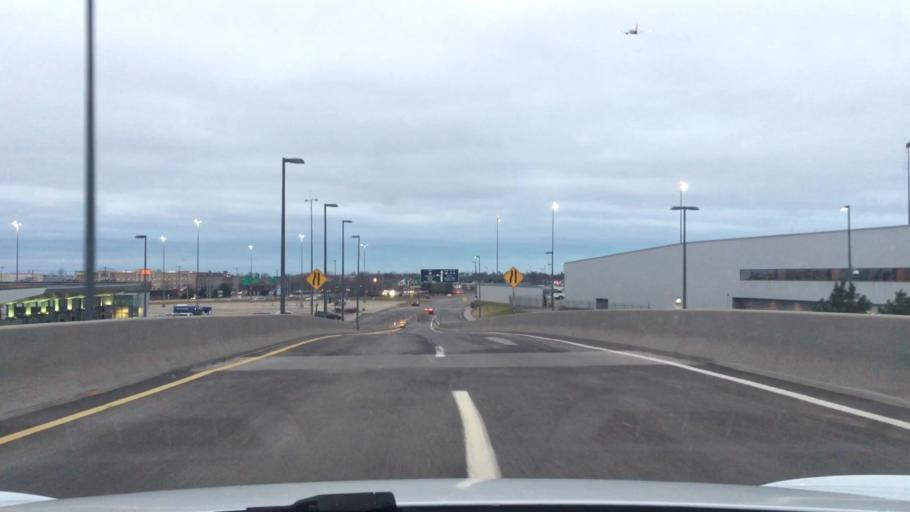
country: US
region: New York
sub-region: Erie County
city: Williamsville
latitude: 42.9333
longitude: -78.7329
